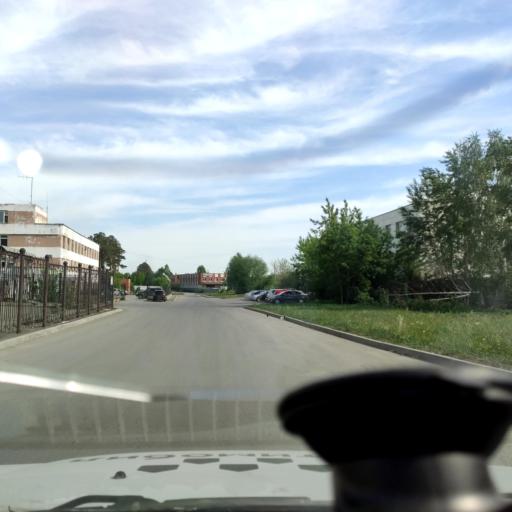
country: RU
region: Sverdlovsk
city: Sovkhoznyy
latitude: 56.7723
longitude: 60.5570
